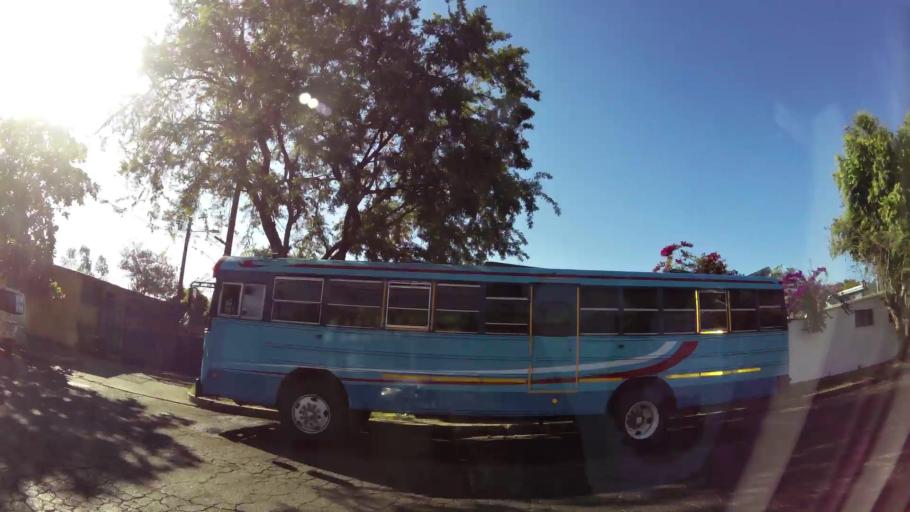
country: SV
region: La Libertad
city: Santa Tecla
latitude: 13.6909
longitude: -89.2881
